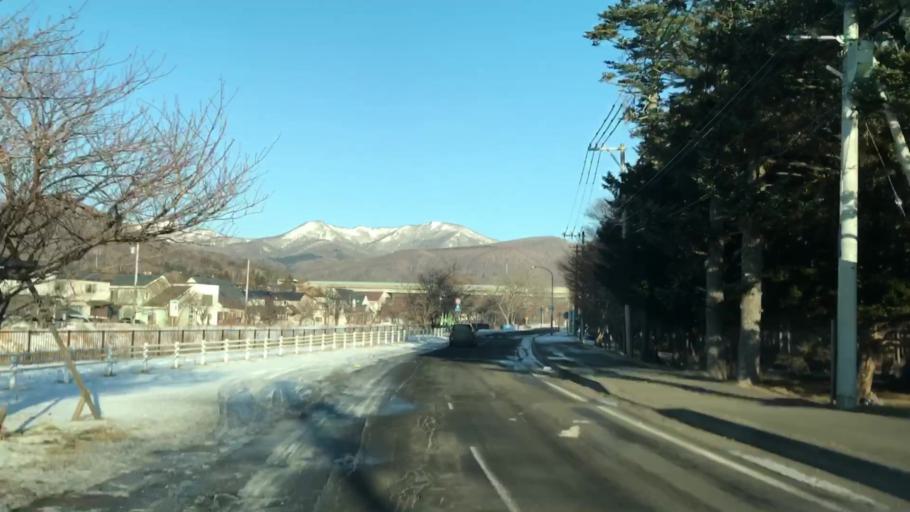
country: JP
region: Hokkaido
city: Muroran
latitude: 42.3871
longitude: 141.0697
